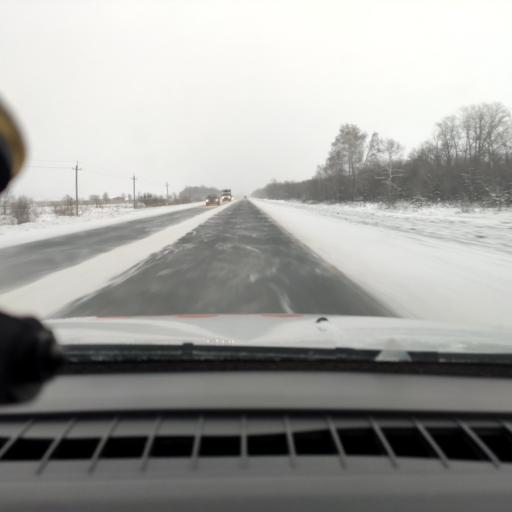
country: RU
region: Samara
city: Kinel'
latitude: 53.2502
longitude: 50.6540
